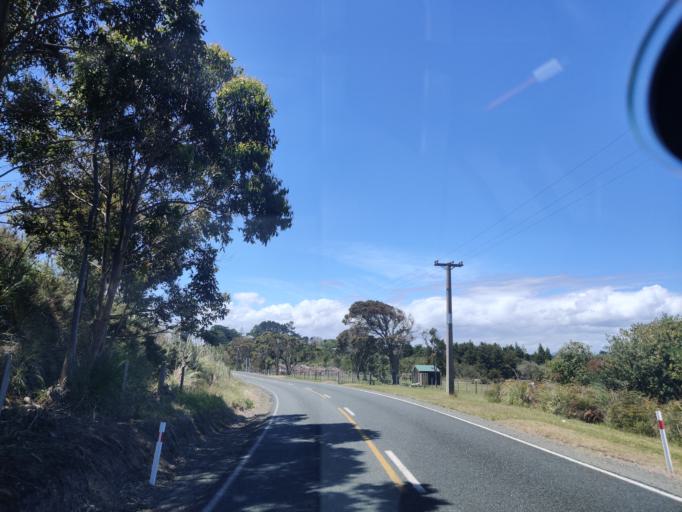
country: NZ
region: Northland
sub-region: Far North District
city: Kaitaia
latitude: -35.0267
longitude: 173.1993
